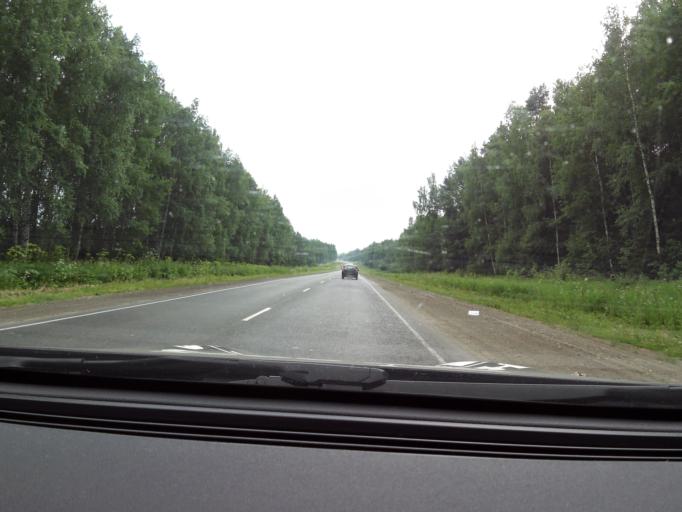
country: RU
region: Perm
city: Kungur
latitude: 57.4381
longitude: 56.8208
